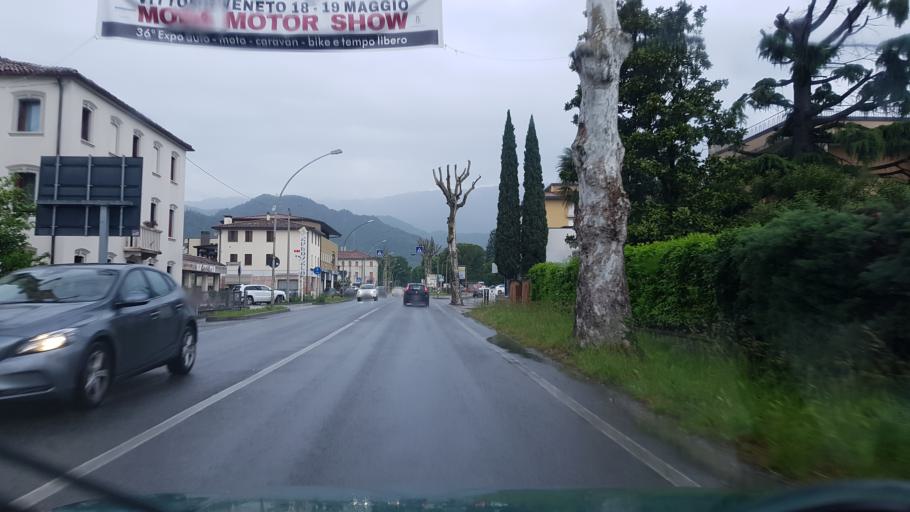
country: IT
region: Veneto
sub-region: Provincia di Treviso
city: Vittorio Veneto
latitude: 45.9719
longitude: 12.3110
